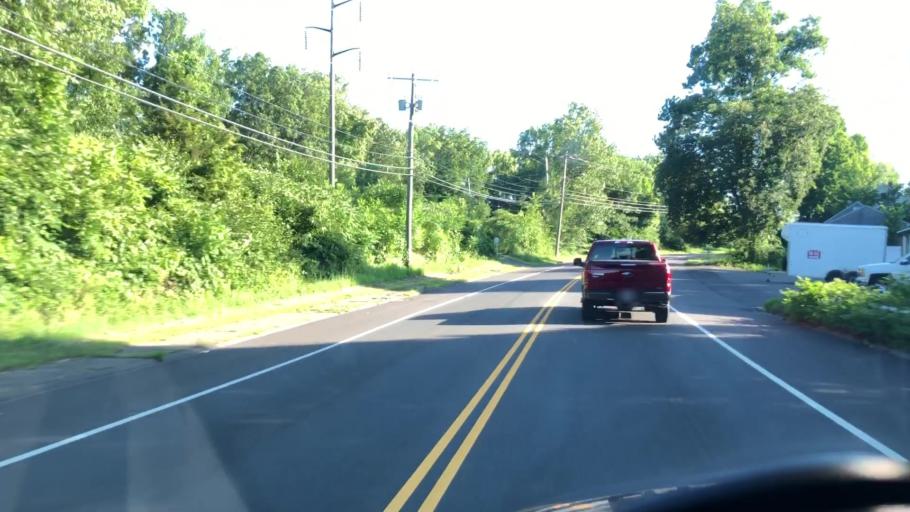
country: US
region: Massachusetts
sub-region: Hampshire County
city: Easthampton
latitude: 42.2789
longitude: -72.6547
